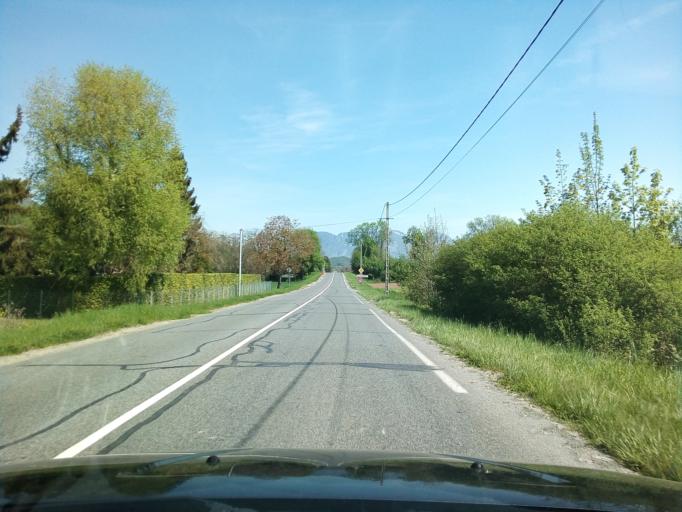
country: FR
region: Rhone-Alpes
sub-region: Departement de l'Isere
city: Barraux
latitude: 45.4050
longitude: 5.9806
